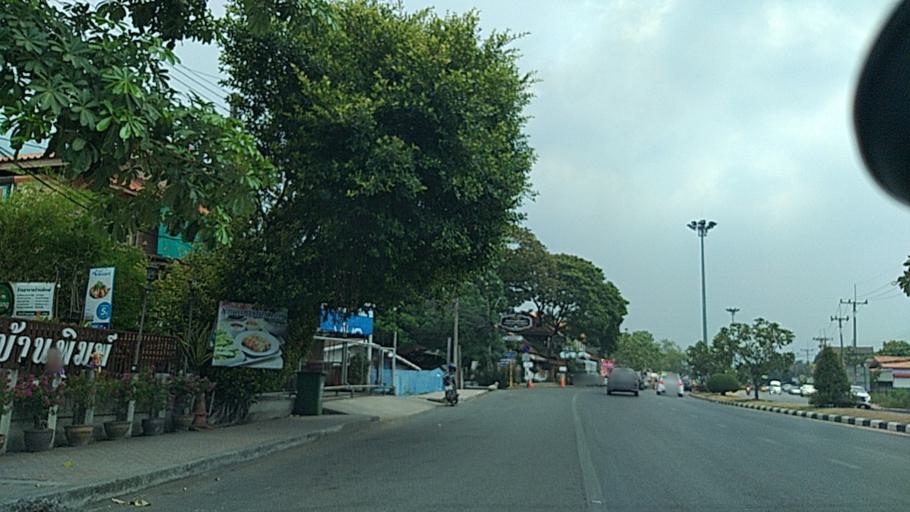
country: TH
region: Phra Nakhon Si Ayutthaya
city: Phra Nakhon Si Ayutthaya
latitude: 14.3490
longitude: 100.5920
